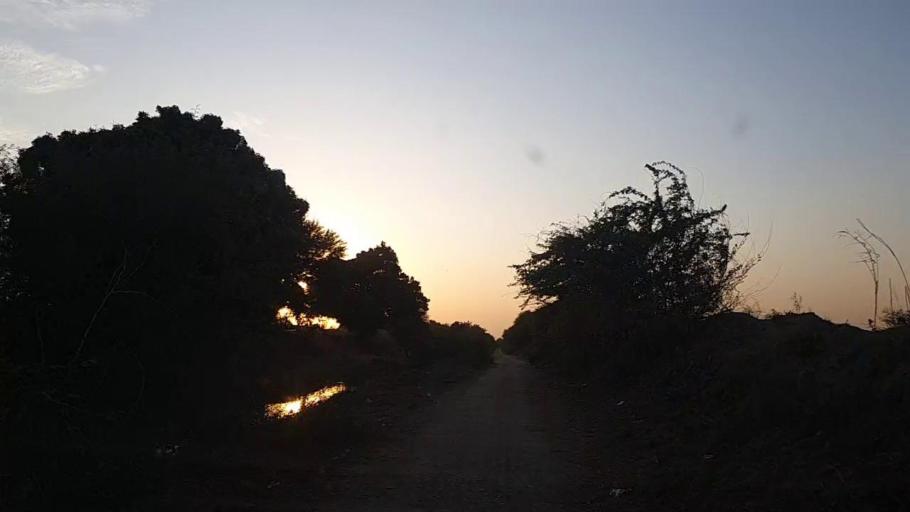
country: PK
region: Sindh
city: Thatta
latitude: 24.7919
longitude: 67.9272
